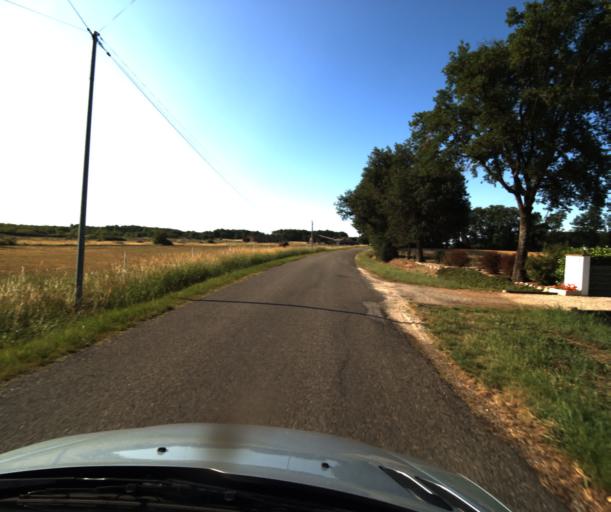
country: FR
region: Midi-Pyrenees
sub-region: Departement du Tarn-et-Garonne
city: Saint-Porquier
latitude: 44.0622
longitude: 1.2081
